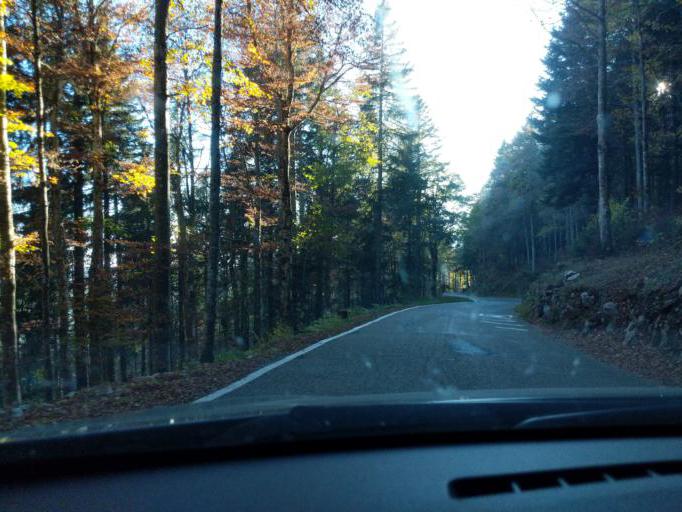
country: CH
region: Bern
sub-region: Jura bernois
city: Saint-Imier
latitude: 47.1146
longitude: 7.0370
